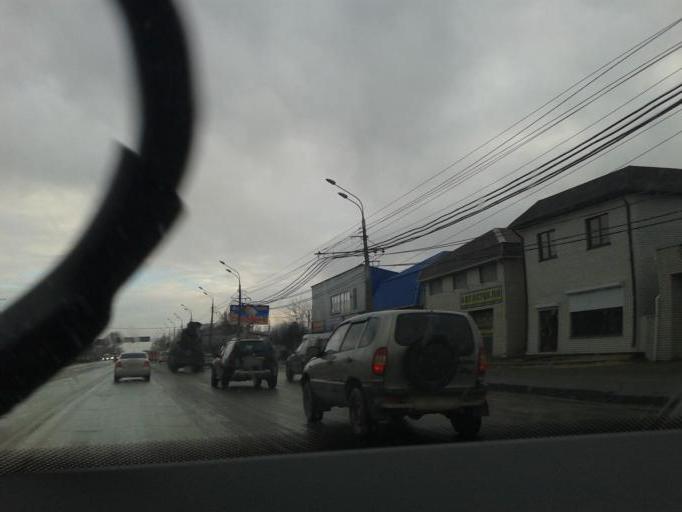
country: RU
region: Volgograd
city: Volgograd
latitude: 48.6937
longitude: 44.4648
